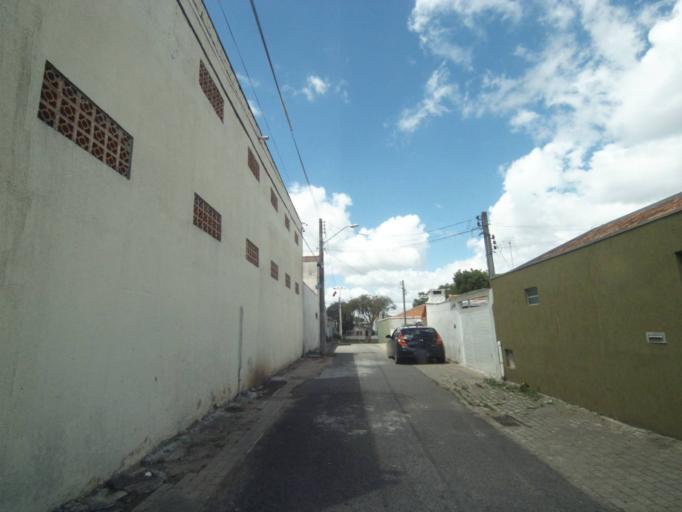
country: BR
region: Parana
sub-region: Curitiba
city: Curitiba
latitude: -25.5059
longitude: -49.3250
